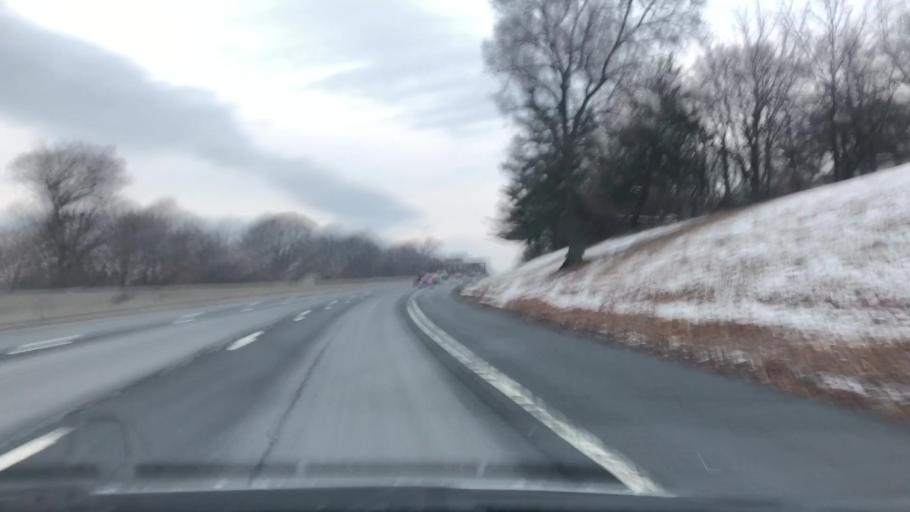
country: US
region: New Jersey
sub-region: Essex County
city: Bloomfield
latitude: 40.8175
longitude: -74.1792
